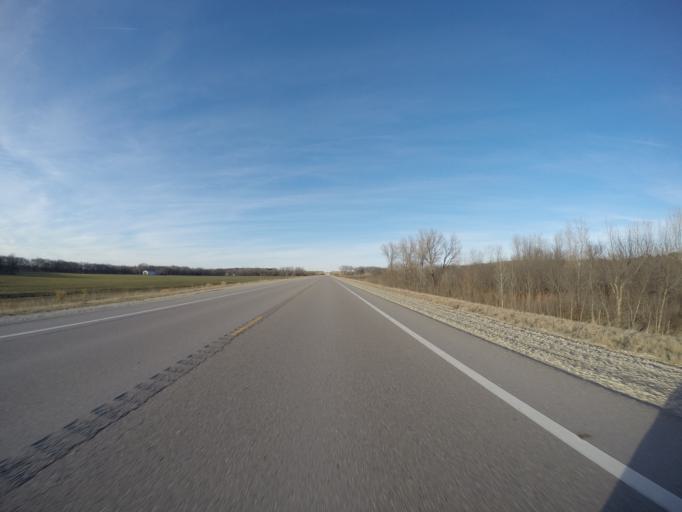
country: US
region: Kansas
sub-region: Marion County
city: Marion
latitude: 38.2702
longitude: -96.9607
